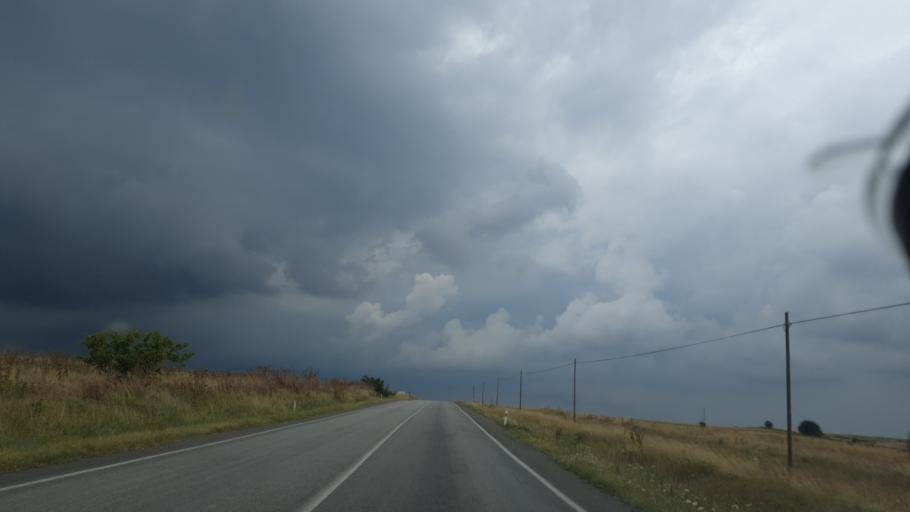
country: TR
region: Tekirdag
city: Hayrabolu
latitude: 41.2189
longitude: 27.0561
